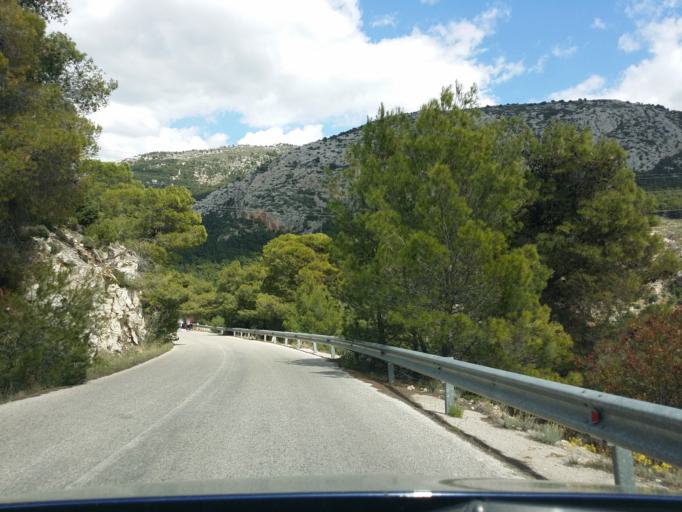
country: GR
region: Attica
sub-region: Nomarchia Dytikis Attikis
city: Fyli
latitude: 38.1199
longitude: 23.6555
